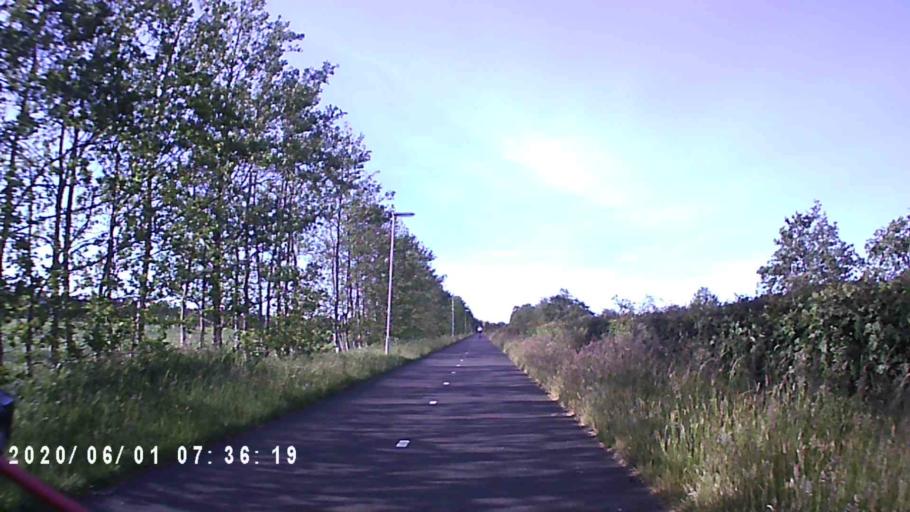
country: NL
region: Friesland
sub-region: Gemeente Dantumadiel
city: Damwald
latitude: 53.3035
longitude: 5.9946
